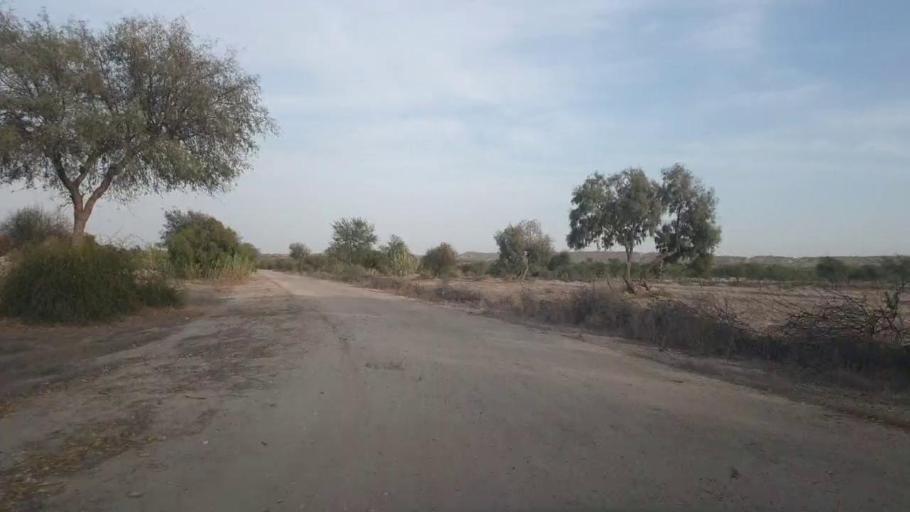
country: PK
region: Sindh
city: Nabisar
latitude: 25.0995
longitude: 69.6688
